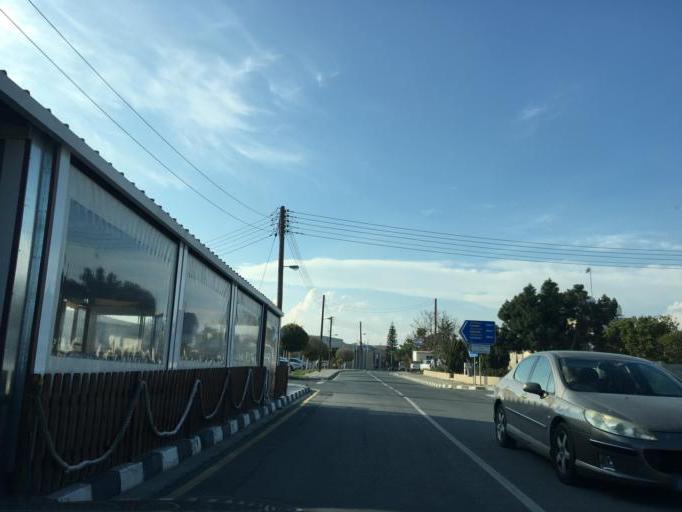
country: CY
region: Larnaka
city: Kofinou
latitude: 34.7286
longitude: 33.3387
